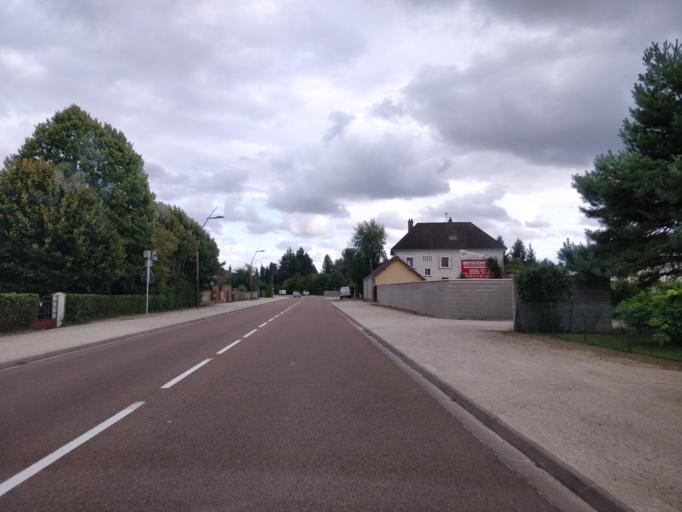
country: FR
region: Champagne-Ardenne
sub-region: Departement de l'Aube
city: Lusigny-sur-Barse
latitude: 48.2495
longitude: 4.2658
